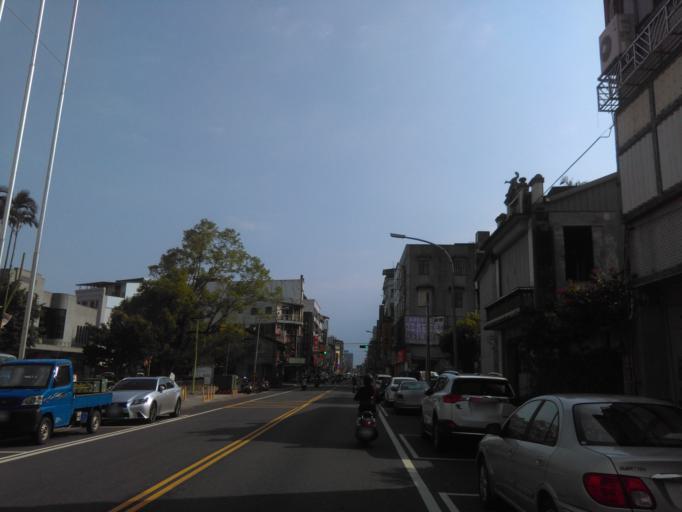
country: TW
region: Taiwan
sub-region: Yilan
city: Yilan
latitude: 24.7519
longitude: 121.7531
